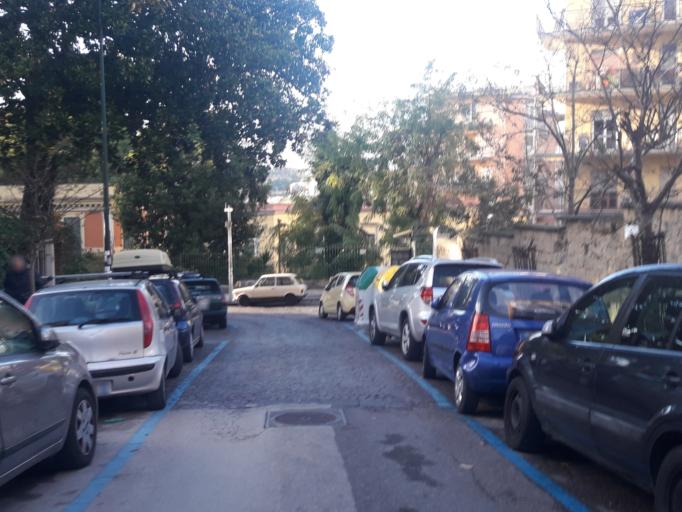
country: IT
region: Campania
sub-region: Provincia di Napoli
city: Napoli
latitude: 40.8463
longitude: 14.2364
